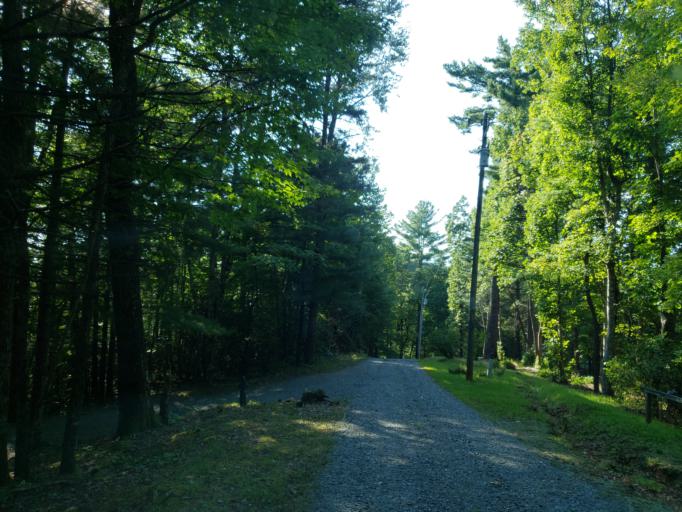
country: US
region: Georgia
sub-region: Fannin County
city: Blue Ridge
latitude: 34.6733
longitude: -84.2635
